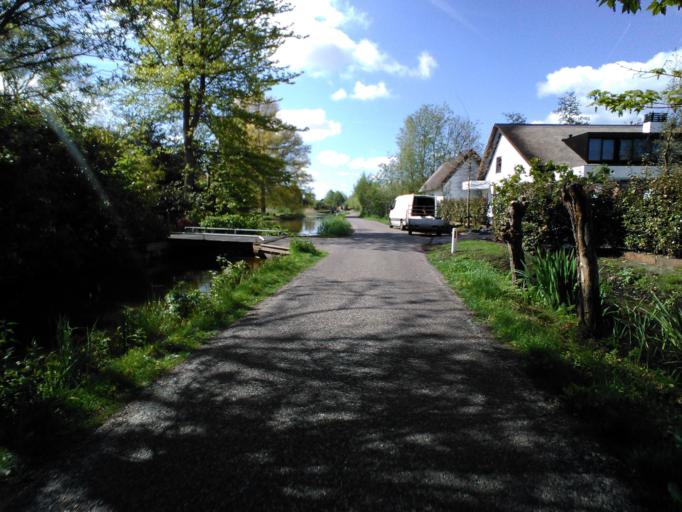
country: NL
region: South Holland
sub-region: Bodegraven-Reeuwijk
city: Reeuwijk
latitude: 52.0373
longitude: 4.7559
